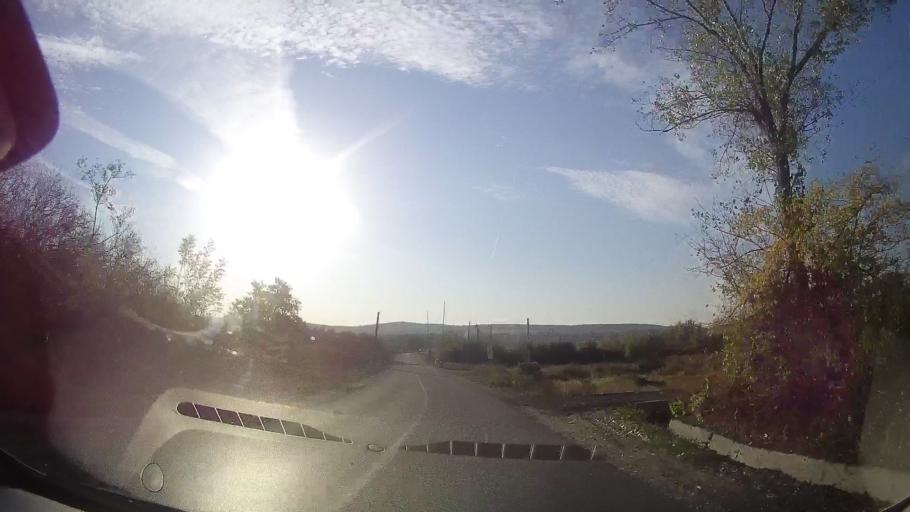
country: RO
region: Timis
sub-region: Comuna Masloc
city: Masloc
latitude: 45.9733
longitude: 21.4704
